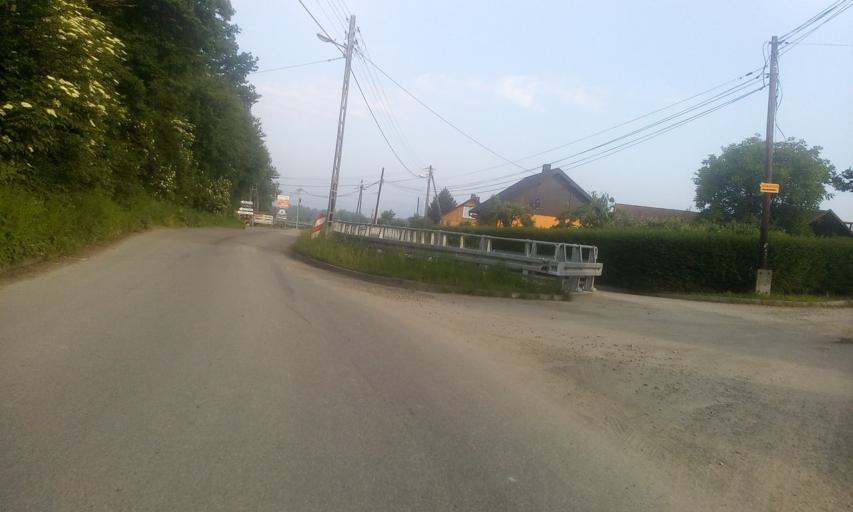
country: PL
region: Lesser Poland Voivodeship
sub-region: Powiat nowosadecki
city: Stary Sacz
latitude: 49.5837
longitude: 20.6639
